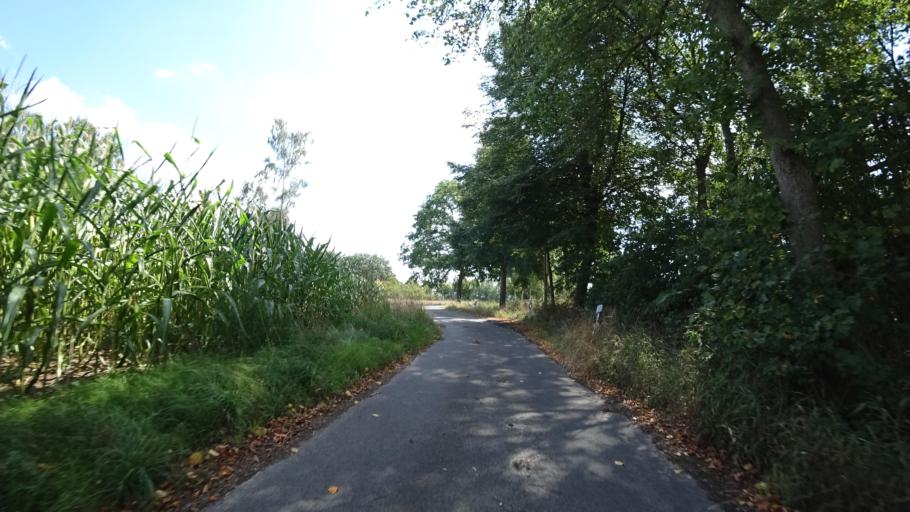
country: DE
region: North Rhine-Westphalia
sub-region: Regierungsbezirk Detmold
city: Rheda-Wiedenbruck
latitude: 51.8777
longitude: 8.2884
